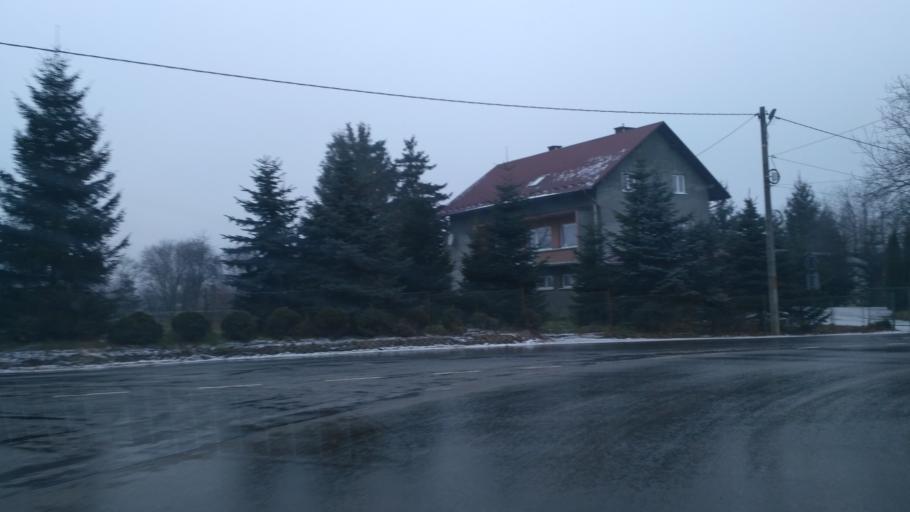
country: PL
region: Subcarpathian Voivodeship
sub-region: Powiat przeworski
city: Gac
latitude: 50.0190
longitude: 22.3932
